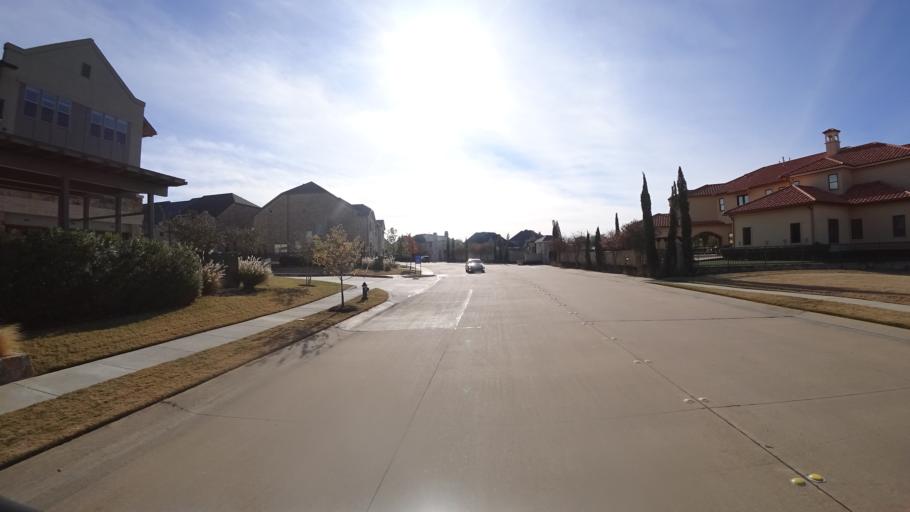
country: US
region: Texas
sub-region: Denton County
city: The Colony
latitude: 33.0348
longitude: -96.8996
